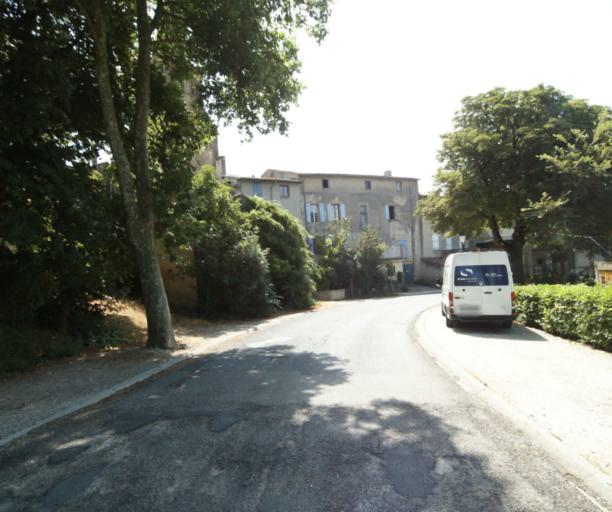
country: FR
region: Midi-Pyrenees
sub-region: Departement de la Haute-Garonne
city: Saint-Felix-Lauragais
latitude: 43.4495
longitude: 1.8869
